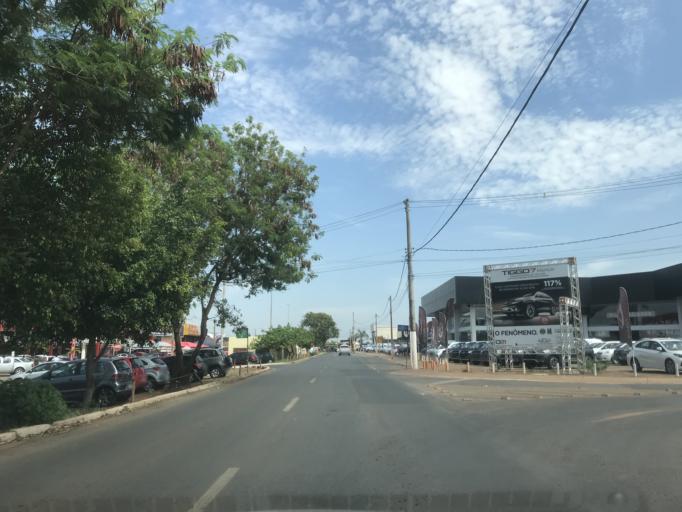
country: BR
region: Federal District
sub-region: Brasilia
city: Brasilia
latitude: -15.7915
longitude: -47.9712
